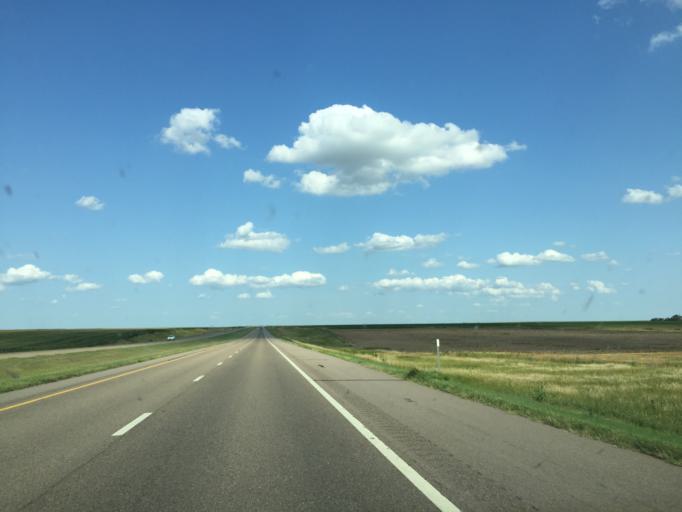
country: US
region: Kansas
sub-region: Trego County
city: WaKeeney
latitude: 39.0231
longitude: -100.0509
